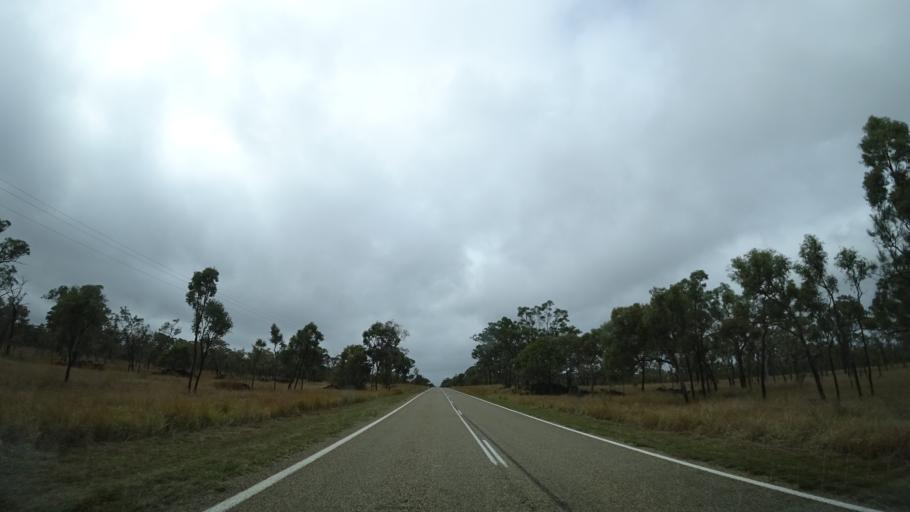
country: AU
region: Queensland
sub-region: Tablelands
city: Ravenshoe
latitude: -18.1511
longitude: 144.7302
